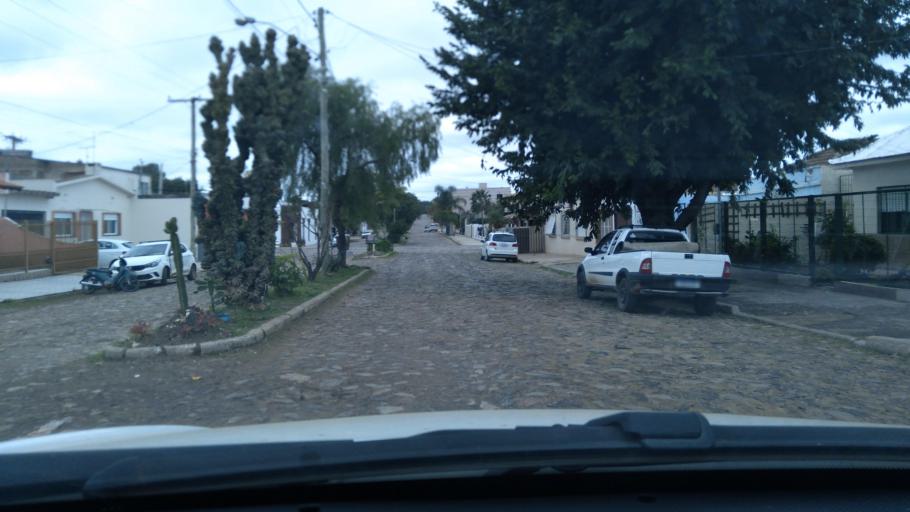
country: BR
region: Rio Grande do Sul
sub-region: Dom Pedrito
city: Dom Pedrito
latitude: -30.9747
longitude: -54.6711
